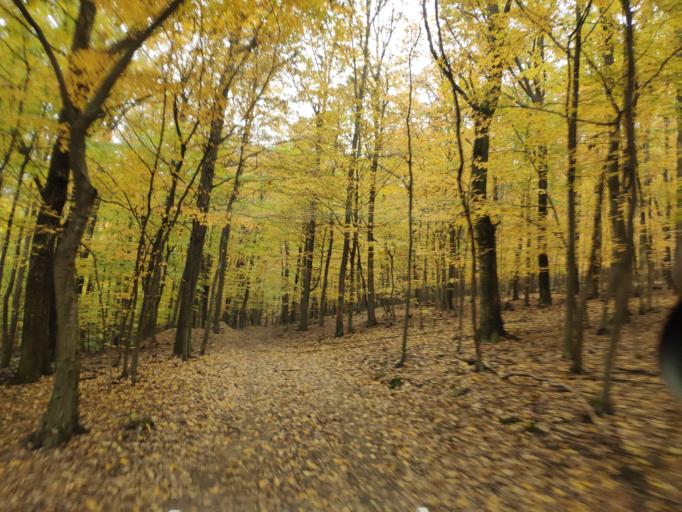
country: SK
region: Kosicky
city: Moldava nad Bodvou
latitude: 48.7165
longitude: 21.0111
